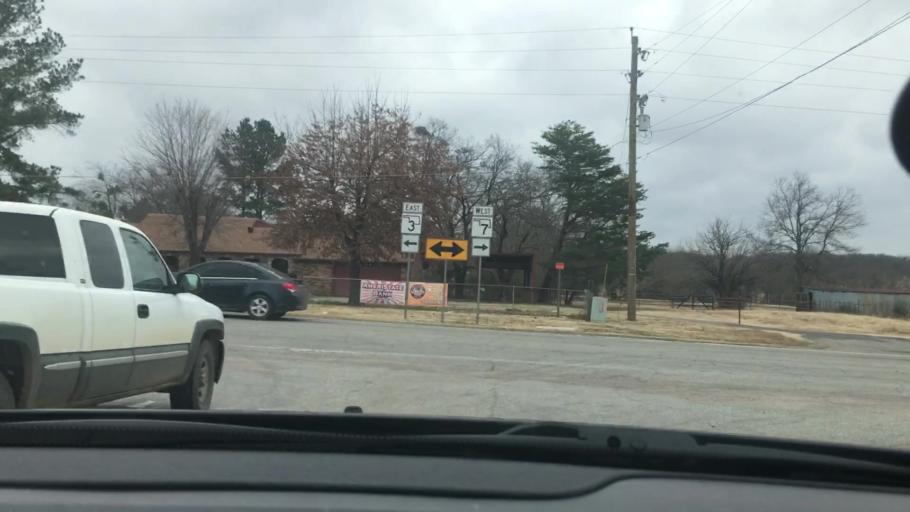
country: US
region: Oklahoma
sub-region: Atoka County
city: Atoka
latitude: 34.3750
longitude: -96.1455
